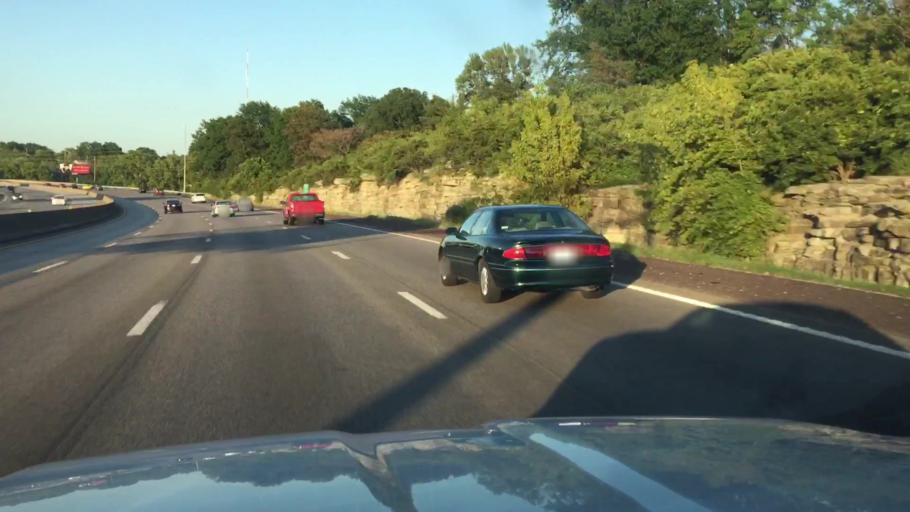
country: US
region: Missouri
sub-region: Saint Louis County
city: Mehlville
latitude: 38.5213
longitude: -90.3245
